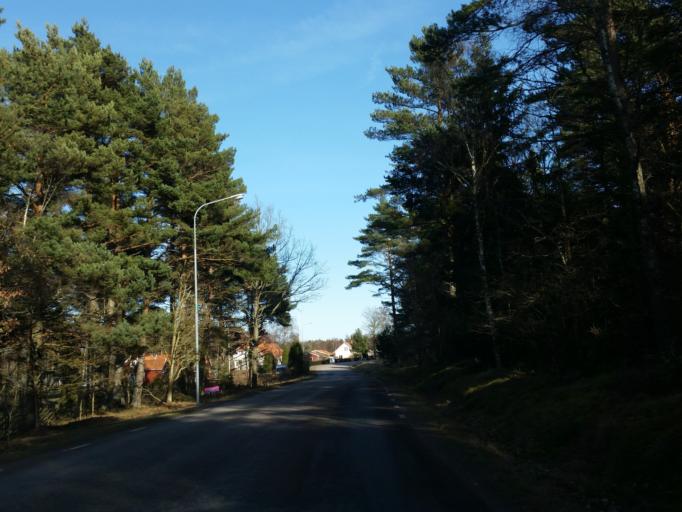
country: SE
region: Kalmar
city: Faerjestaden
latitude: 56.7829
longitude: 16.4404
